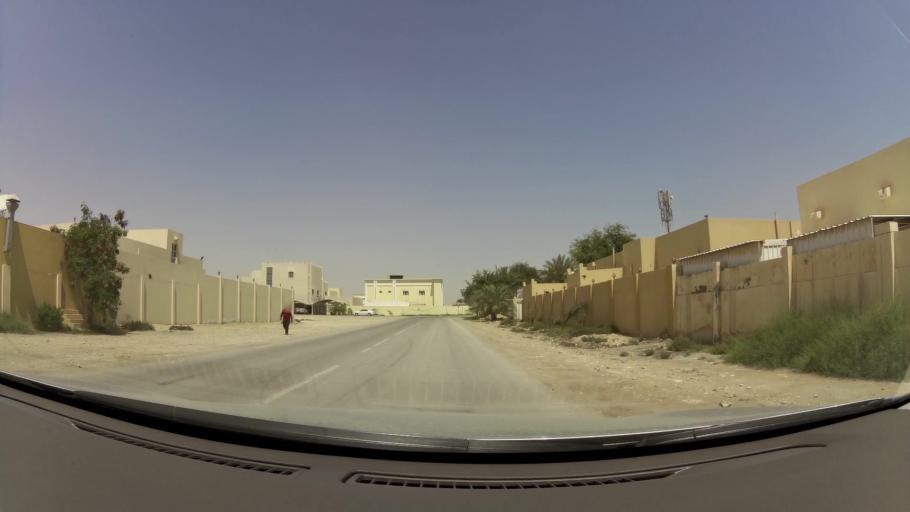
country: QA
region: Baladiyat Umm Salal
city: Umm Salal Muhammad
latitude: 25.3735
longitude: 51.4749
